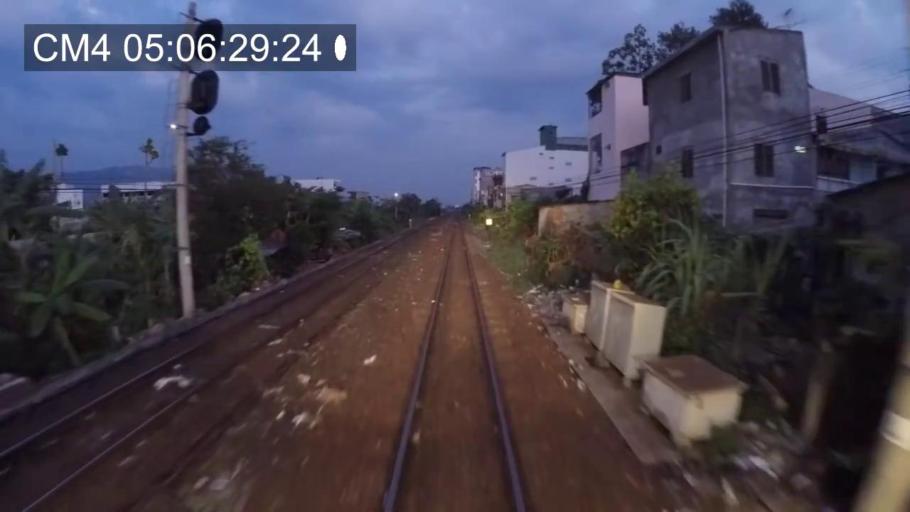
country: VN
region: Khanh Hoa
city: Nha Trang
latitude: 12.2783
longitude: 109.1804
